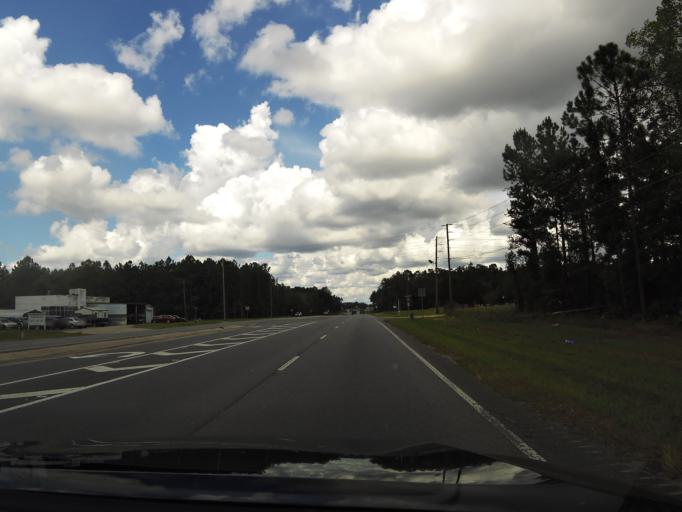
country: US
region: Georgia
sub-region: Charlton County
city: Folkston
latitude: 30.8467
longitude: -82.0077
